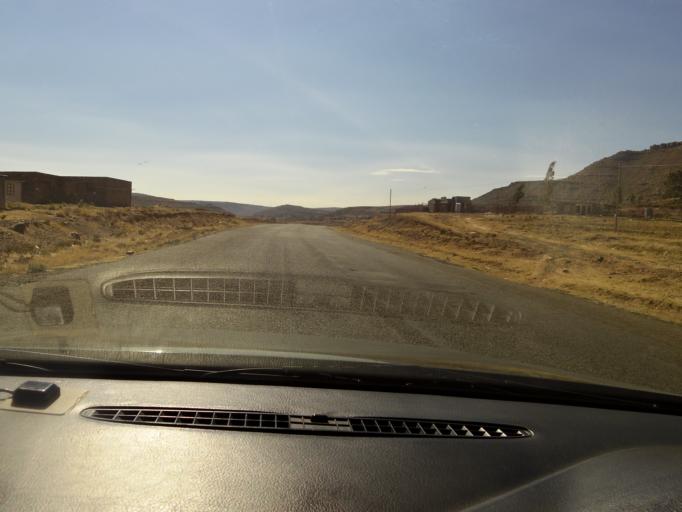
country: LS
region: Quthing
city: Quthing
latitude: -30.3344
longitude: 27.5337
